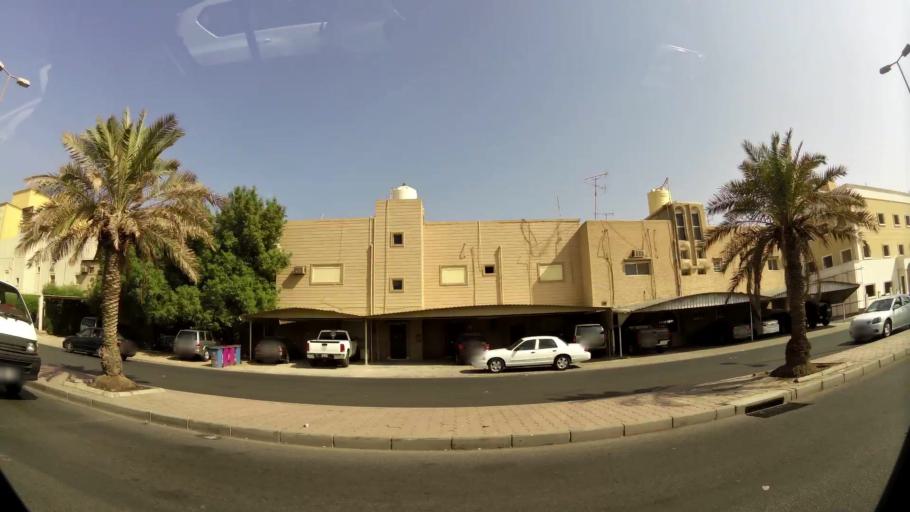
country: KW
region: Al Ahmadi
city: Al Fahahil
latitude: 29.0888
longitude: 48.1225
